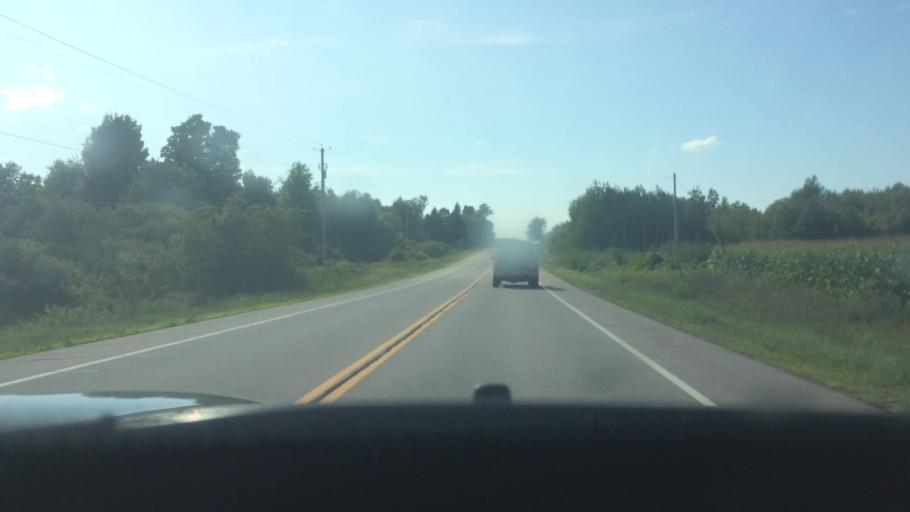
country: US
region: New York
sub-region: Franklin County
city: Malone
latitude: 44.8519
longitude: -74.2091
